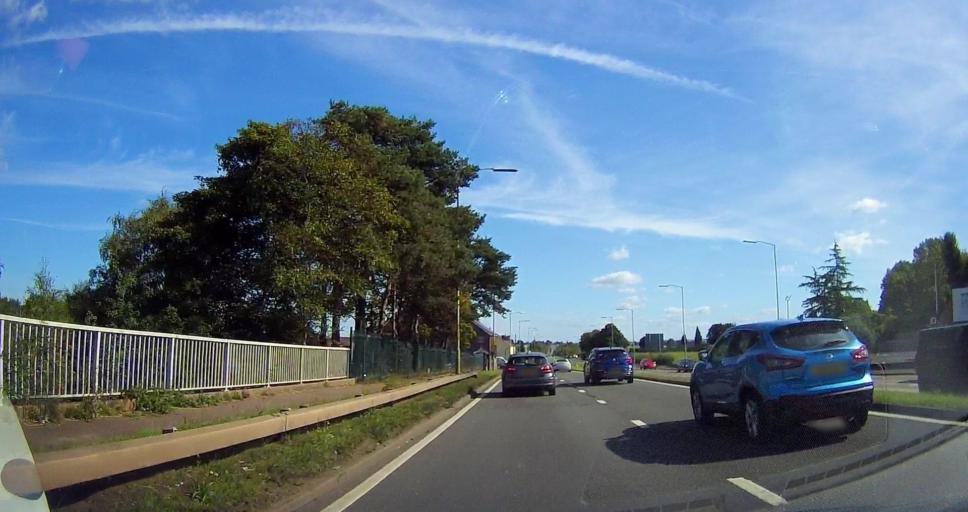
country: GB
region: England
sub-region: Staffordshire
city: Chasetown
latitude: 52.6563
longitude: -1.9203
